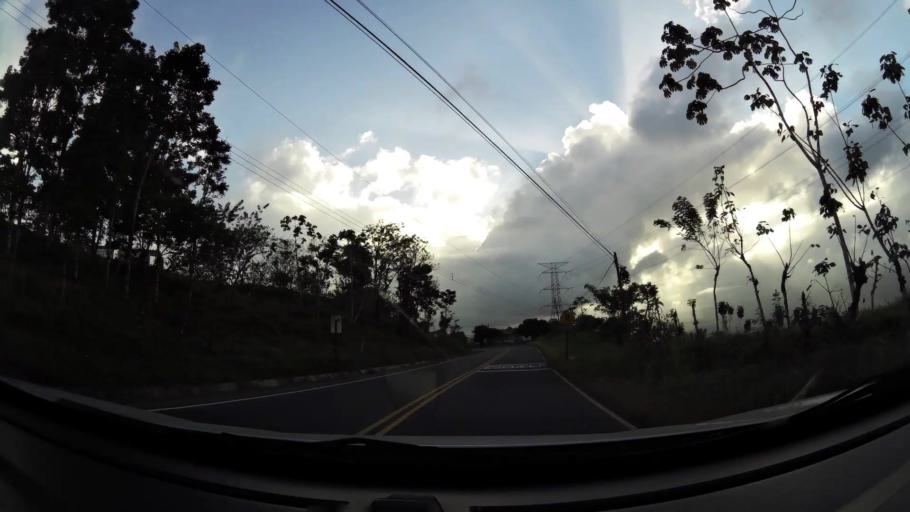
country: CR
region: Limon
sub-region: Canton de Siquirres
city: Siquirres
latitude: 10.0138
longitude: -83.5647
